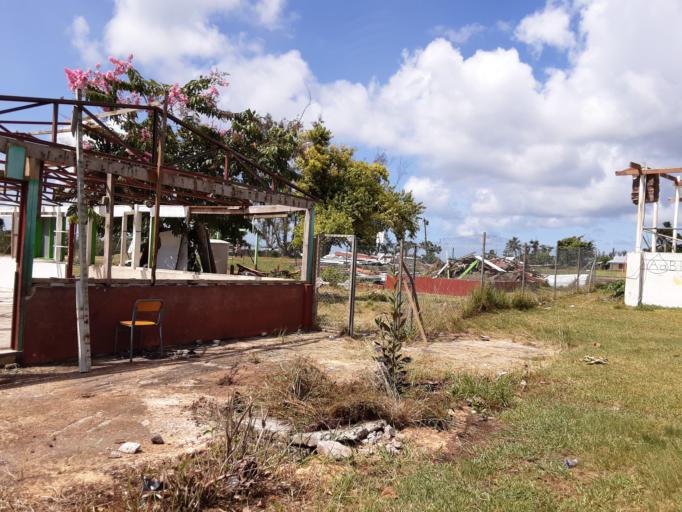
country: VU
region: Sanma
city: Luganville
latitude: -15.5096
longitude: 167.1909
